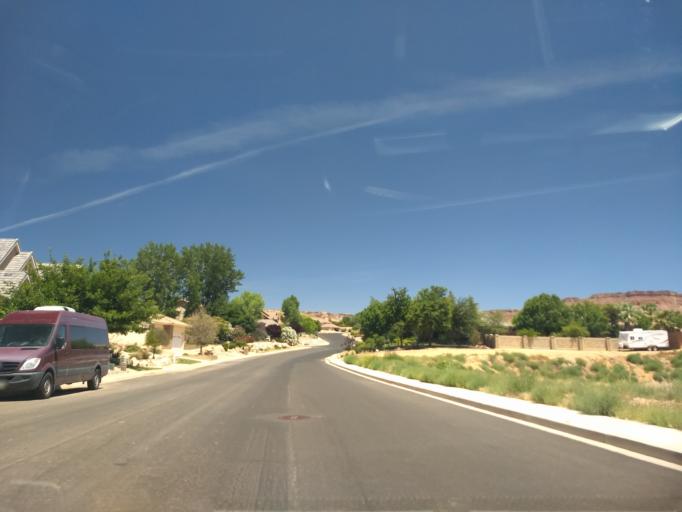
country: US
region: Utah
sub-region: Washington County
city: Washington
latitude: 37.0889
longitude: -113.4914
